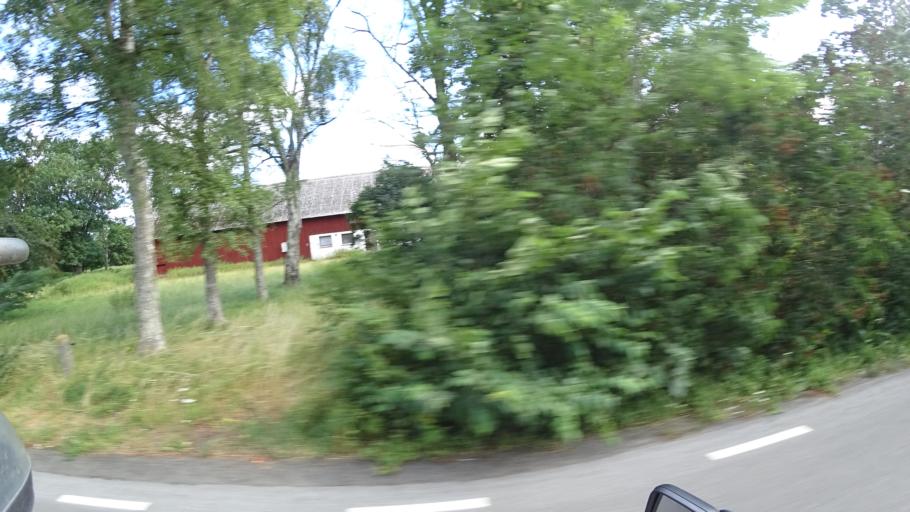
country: SE
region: Skane
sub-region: Kristianstads Kommun
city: Norra Asum
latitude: 55.9712
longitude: 14.1075
